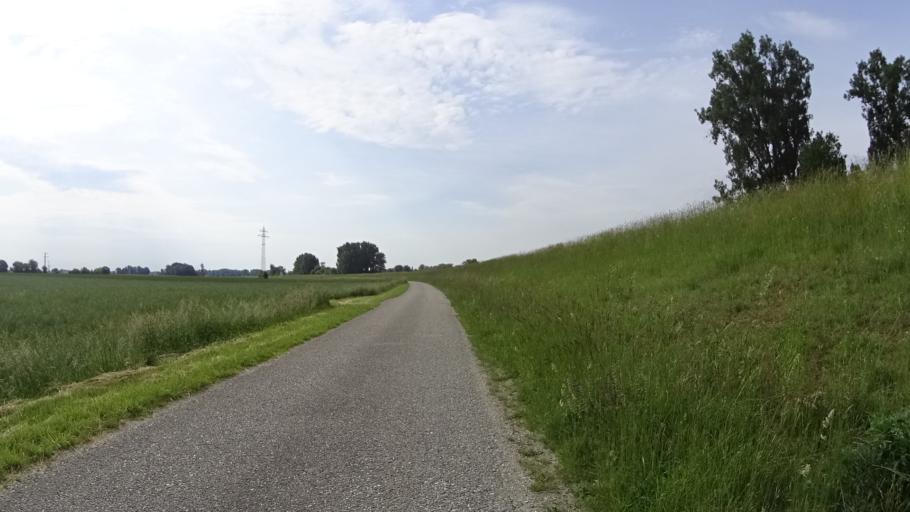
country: DE
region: Bavaria
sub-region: Lower Bavaria
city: Irlbach
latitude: 48.8427
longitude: 12.7686
